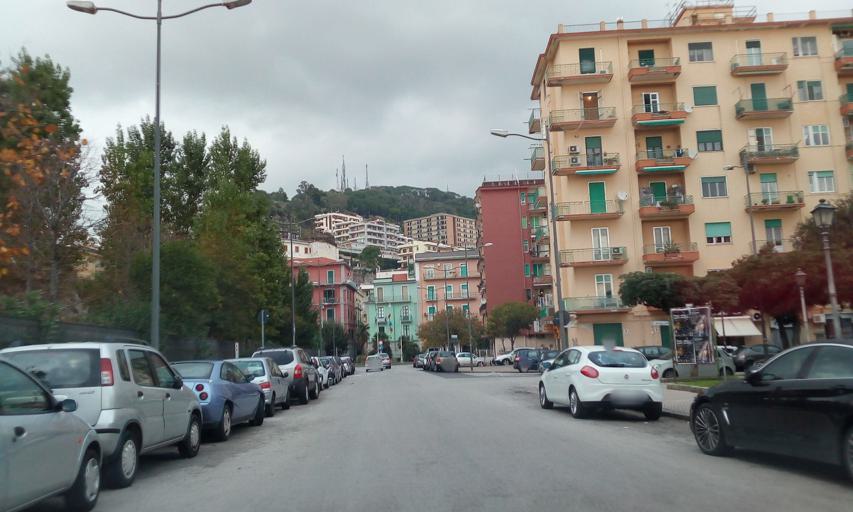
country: IT
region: Campania
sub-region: Provincia di Salerno
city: Salerno
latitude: 40.6708
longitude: 14.7808
